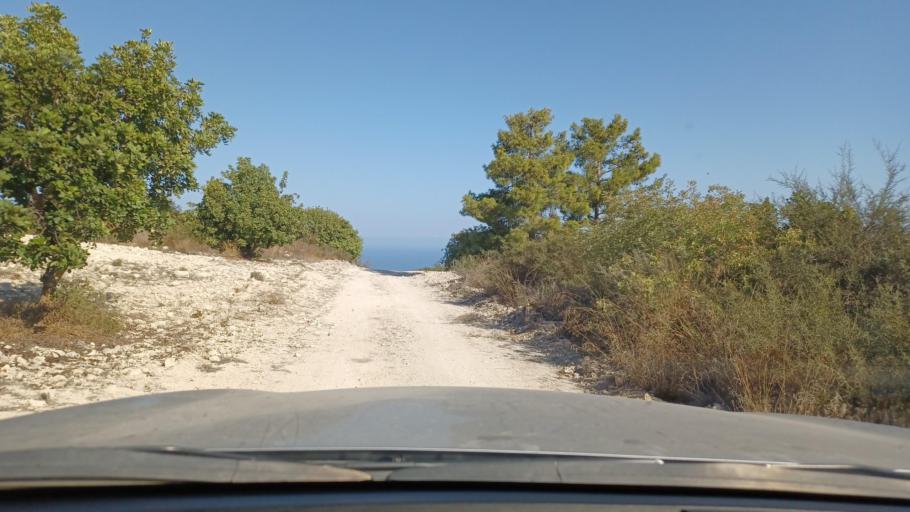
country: CY
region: Pafos
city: Polis
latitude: 35.0095
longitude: 32.4857
